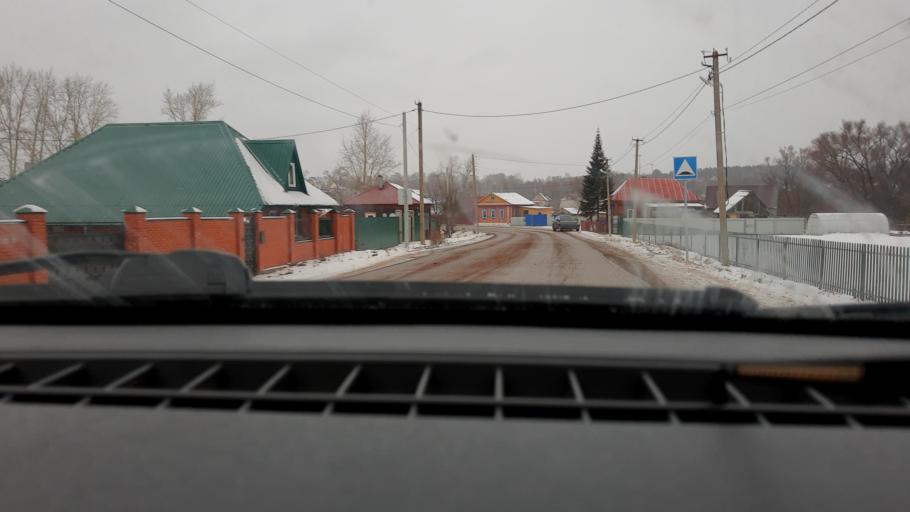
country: RU
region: Bashkortostan
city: Kabakovo
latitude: 54.7037
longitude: 56.2466
